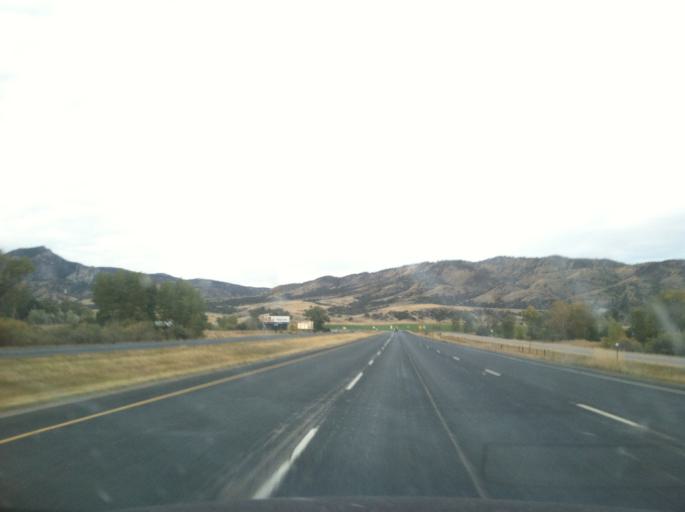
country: US
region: Montana
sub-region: Jefferson County
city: Whitehall
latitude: 45.8698
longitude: -111.9487
